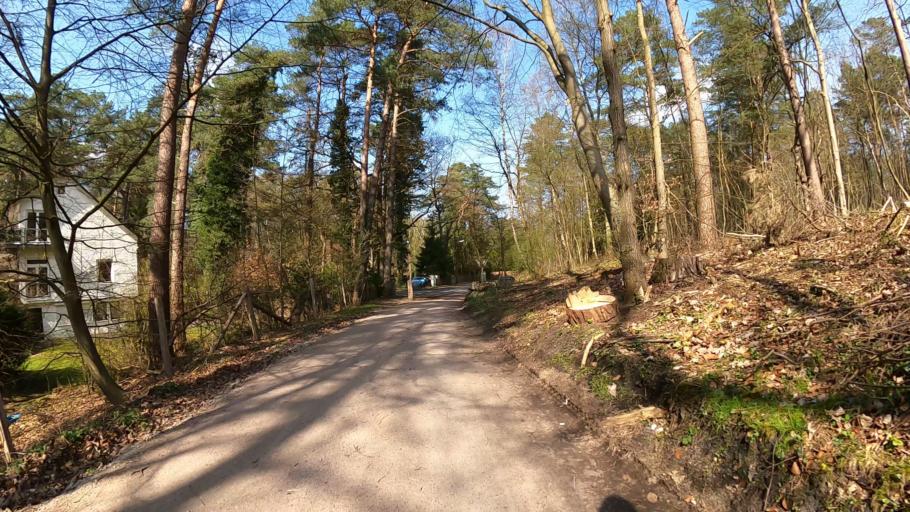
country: DE
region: Lower Saxony
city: Neu Wulmstorf
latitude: 53.4611
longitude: 9.8798
